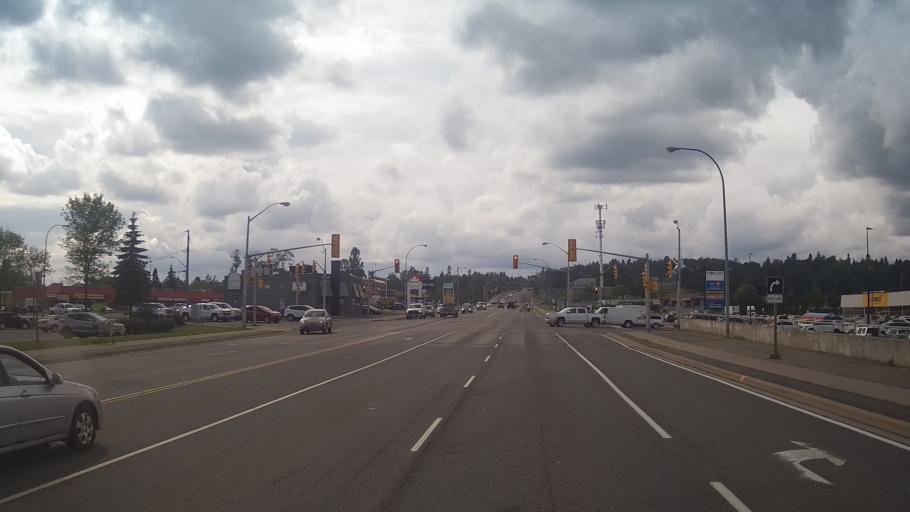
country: CA
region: Ontario
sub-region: Thunder Bay District
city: Thunder Bay
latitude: 48.4512
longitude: -89.2527
